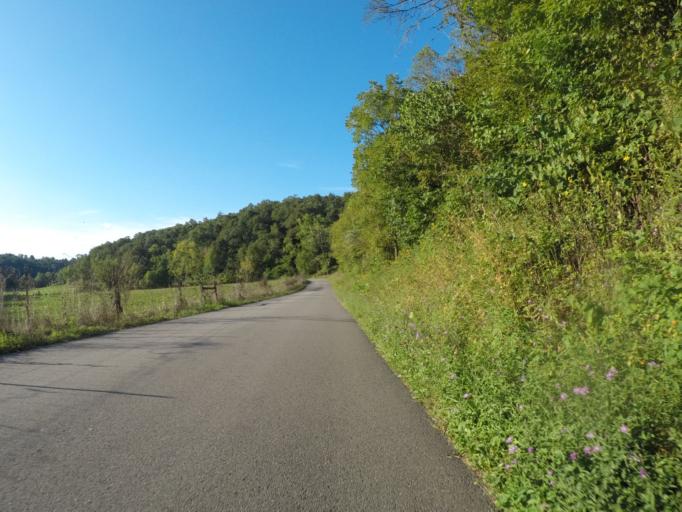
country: US
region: Ohio
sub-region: Lawrence County
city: Coal Grove
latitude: 38.5451
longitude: -82.5504
